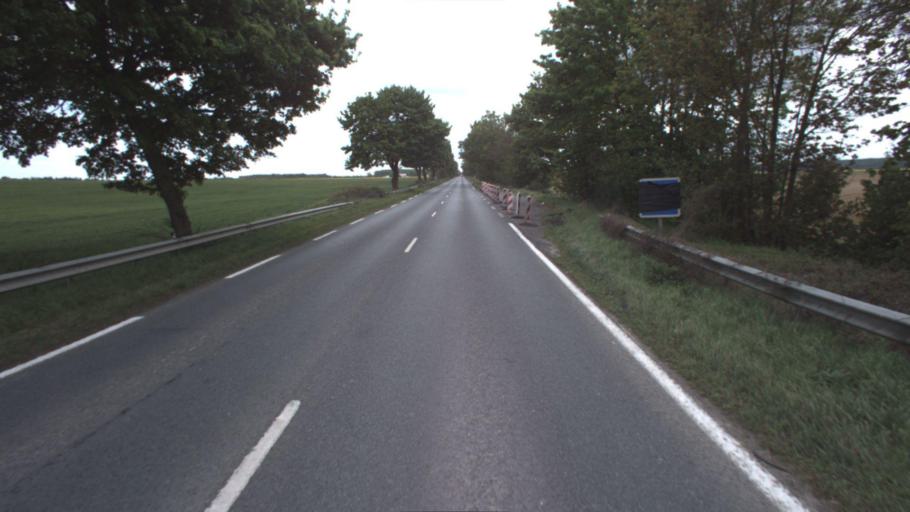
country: FR
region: Picardie
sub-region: Departement de l'Oise
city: Le Plessis-Belleville
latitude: 49.0753
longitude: 2.7659
